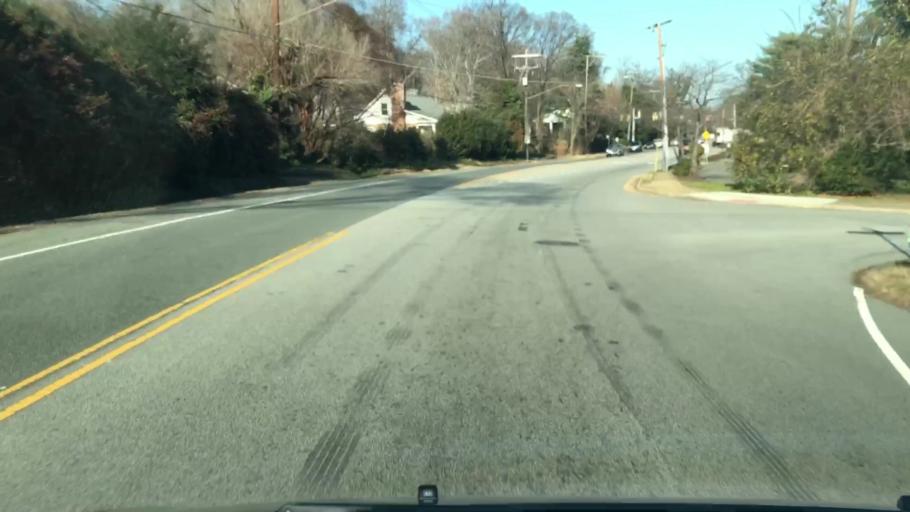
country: US
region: Virginia
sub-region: Fairfax County
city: Belle Haven
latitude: 38.7796
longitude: -77.0630
